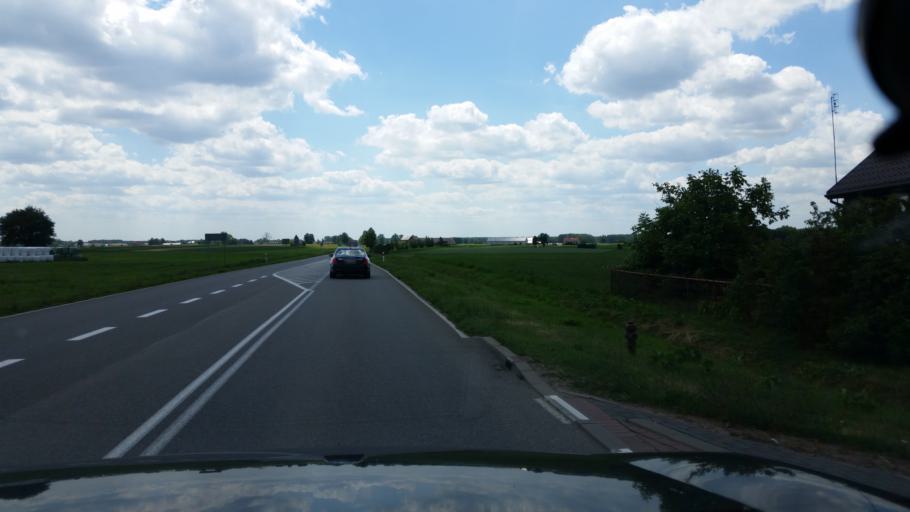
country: PL
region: Masovian Voivodeship
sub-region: Powiat ostrolecki
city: Czerwin
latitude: 52.9373
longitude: 21.8843
